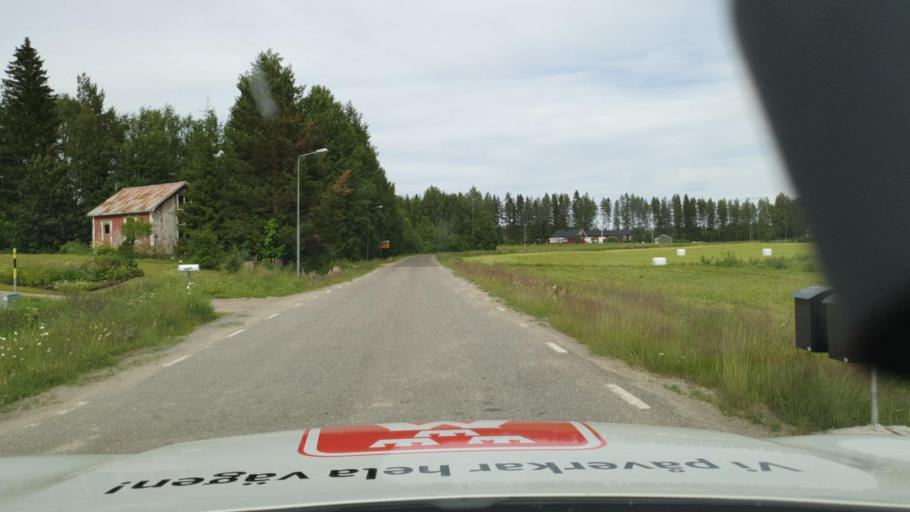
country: SE
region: Vaesterbotten
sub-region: Skelleftea Kommun
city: Viken
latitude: 64.4986
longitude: 20.9102
